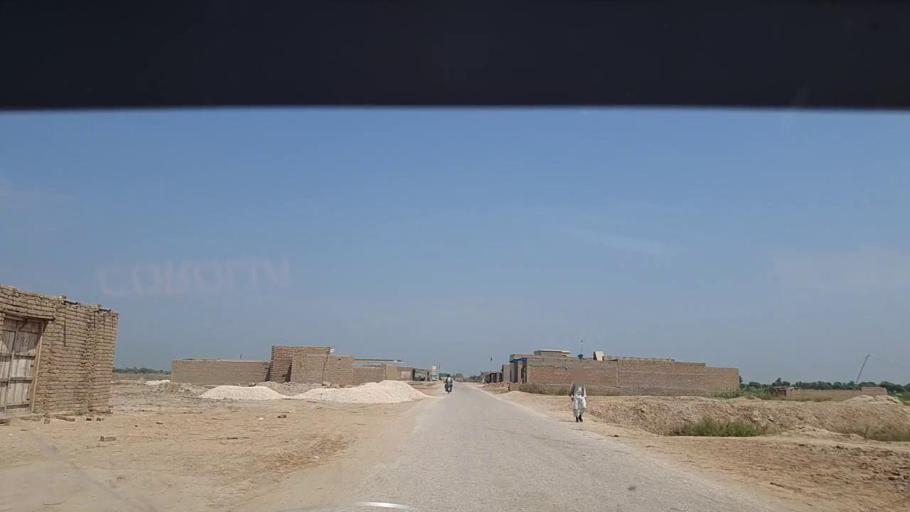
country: PK
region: Sindh
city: Thul
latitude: 28.1230
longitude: 68.8161
